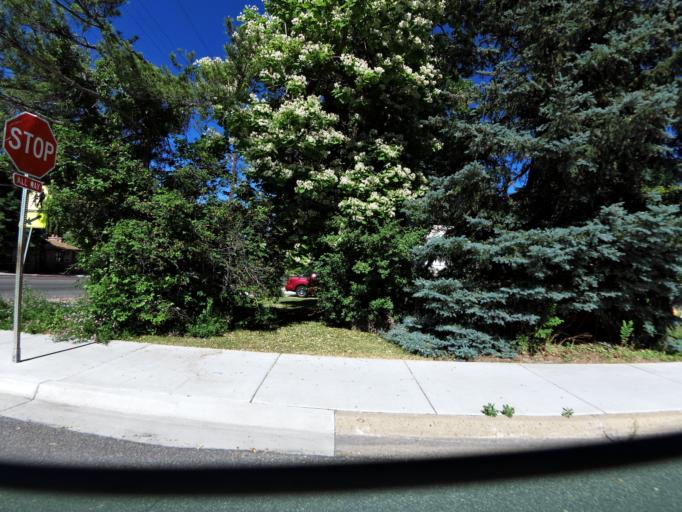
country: US
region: Utah
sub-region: Weber County
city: South Ogden
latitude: 41.2058
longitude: -111.9454
